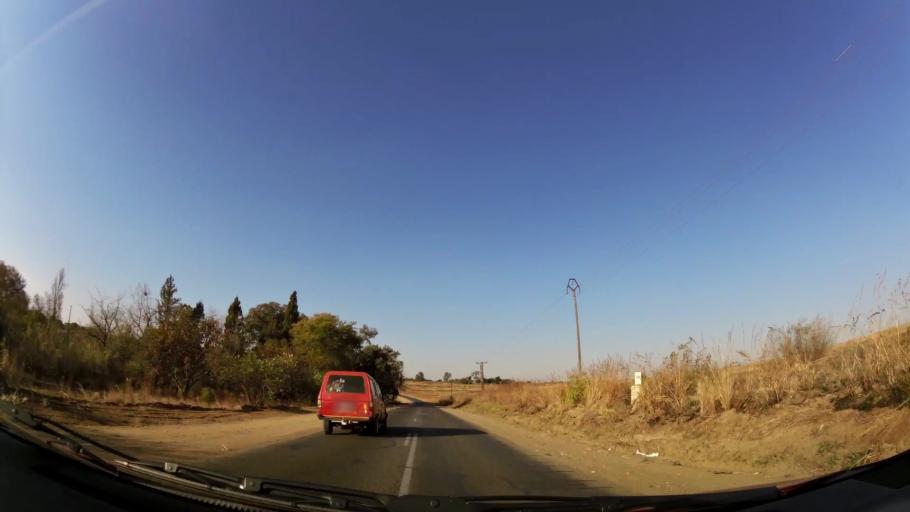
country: ZA
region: Gauteng
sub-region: West Rand District Municipality
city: Muldersdriseloop
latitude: -26.0058
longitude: 27.9102
